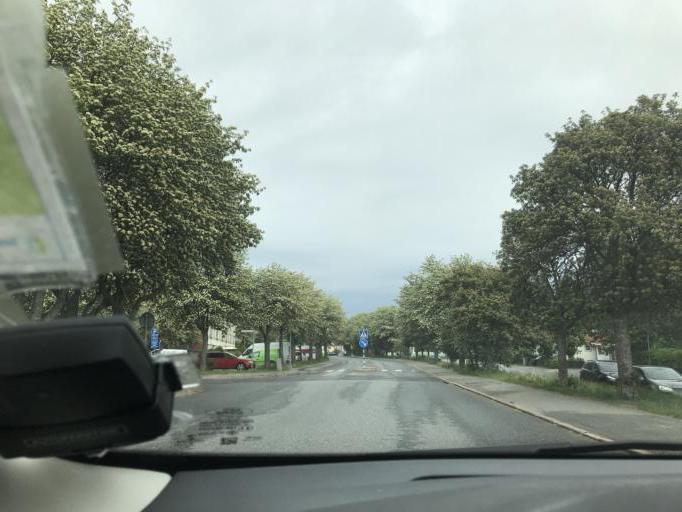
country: SE
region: Stockholm
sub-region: Botkyrka Kommun
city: Tumba
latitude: 59.2043
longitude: 17.8329
